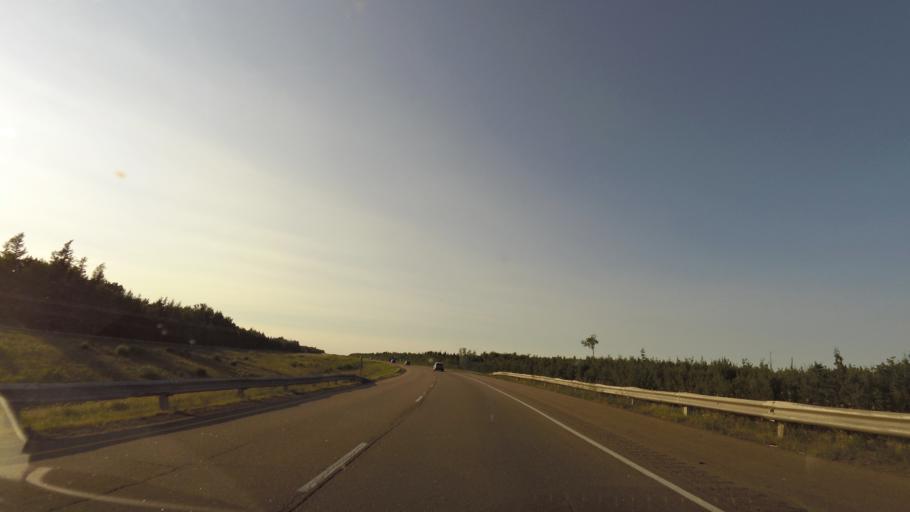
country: CA
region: New Brunswick
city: Dieppe
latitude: 46.1080
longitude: -64.6094
